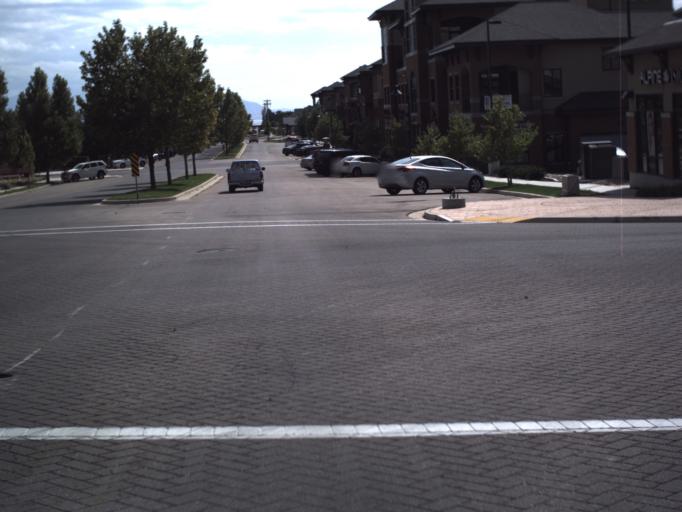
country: US
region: Utah
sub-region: Utah County
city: Lehi
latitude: 40.4313
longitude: -111.8498
